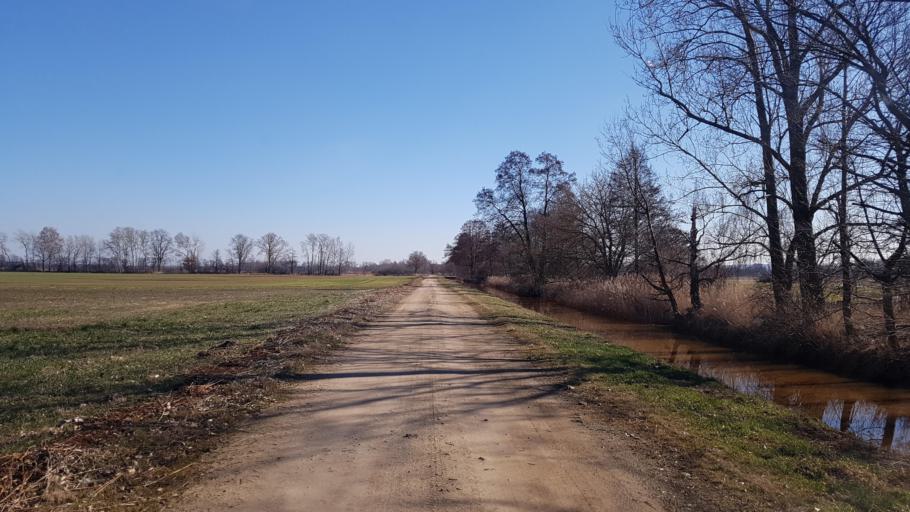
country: DE
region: Brandenburg
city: Hirschfeld
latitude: 51.4156
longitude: 13.6317
